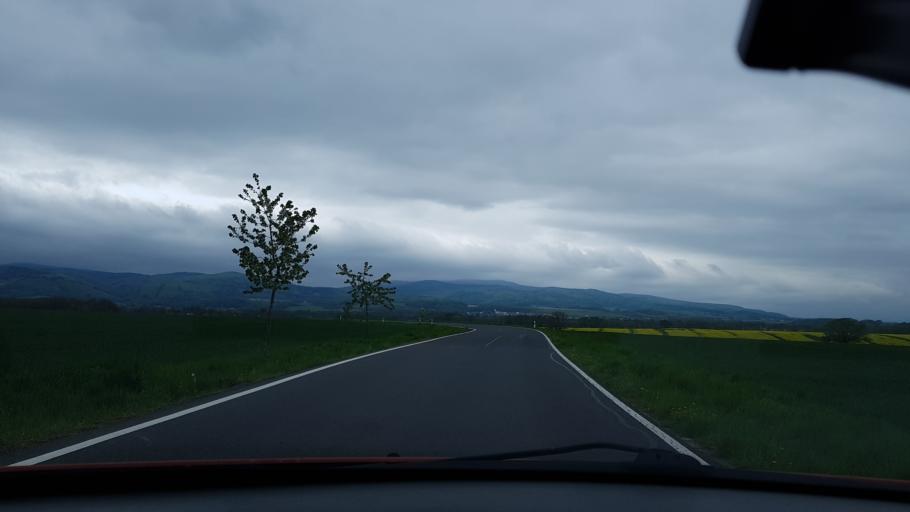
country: CZ
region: Olomoucky
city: Javornik
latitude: 50.3877
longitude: 17.0645
